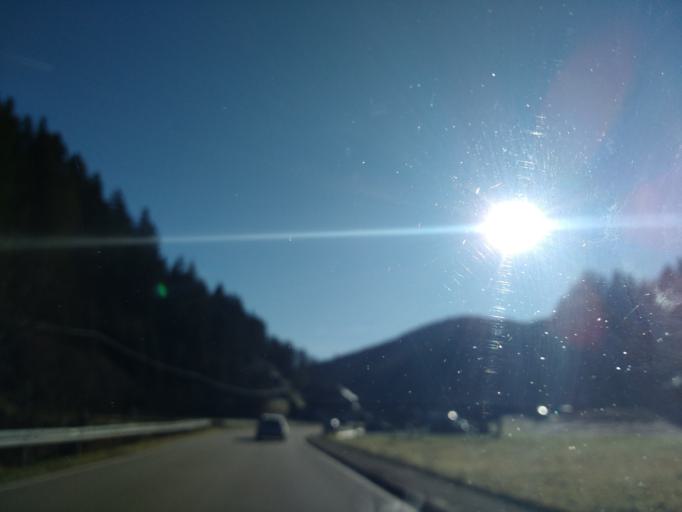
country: DE
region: Baden-Wuerttemberg
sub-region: Karlsruhe Region
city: Bad Rippoldsau-Schapbach
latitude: 48.4409
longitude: 8.3142
